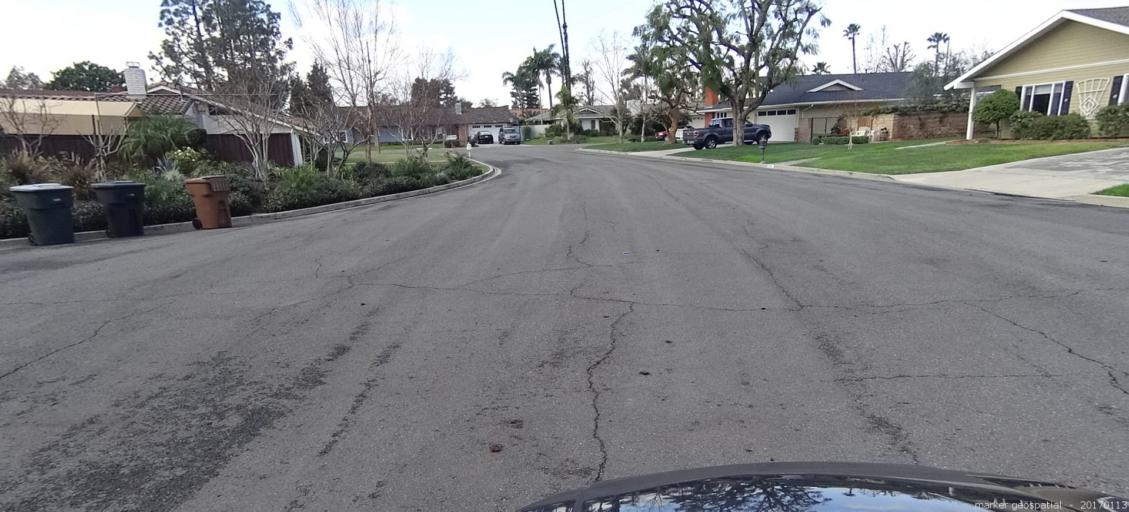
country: US
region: California
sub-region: Orange County
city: Yorba Linda
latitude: 33.8765
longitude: -117.7965
